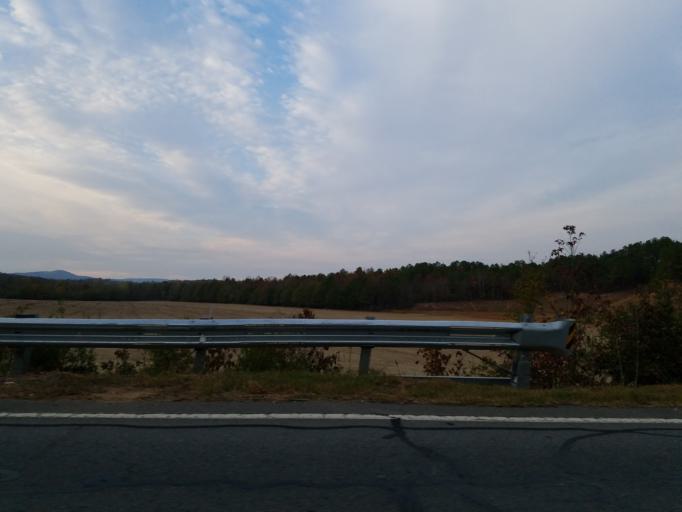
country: US
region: Georgia
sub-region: Gordon County
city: Calhoun
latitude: 34.5953
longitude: -84.9325
